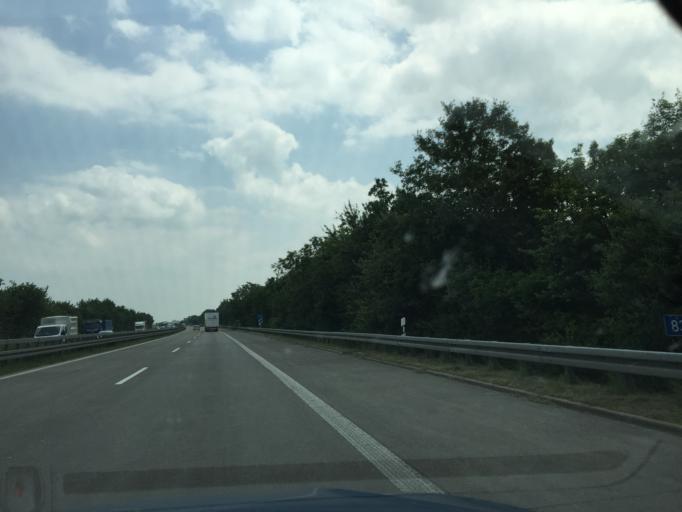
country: DE
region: Baden-Wuerttemberg
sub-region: Tuebingen Region
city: Nerenstetten
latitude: 48.5003
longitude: 10.0836
